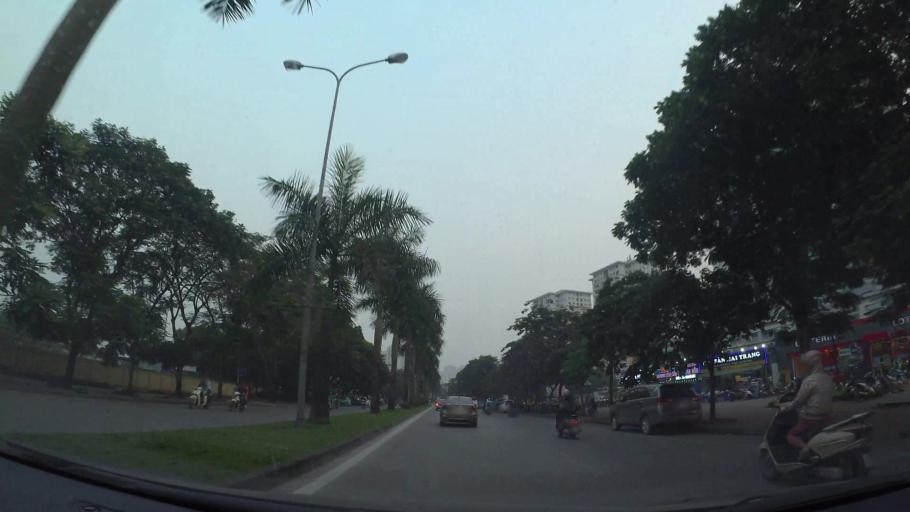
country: VN
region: Ha Noi
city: Ha Dong
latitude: 20.9746
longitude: 105.7897
